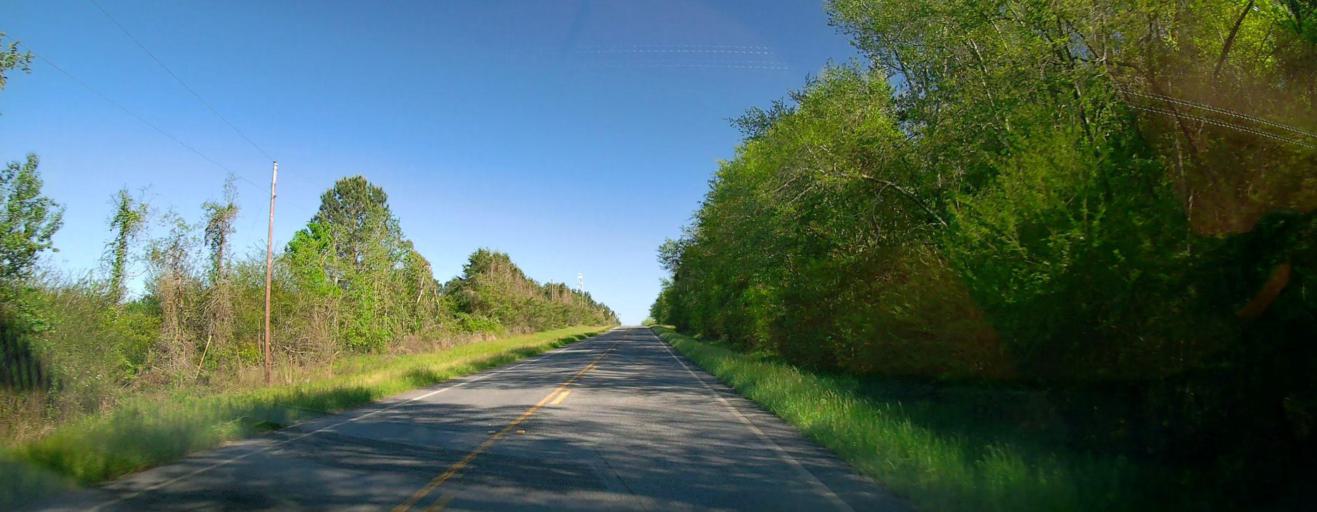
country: US
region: Georgia
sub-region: Wilcox County
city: Rochelle
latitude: 32.0044
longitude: -83.4843
